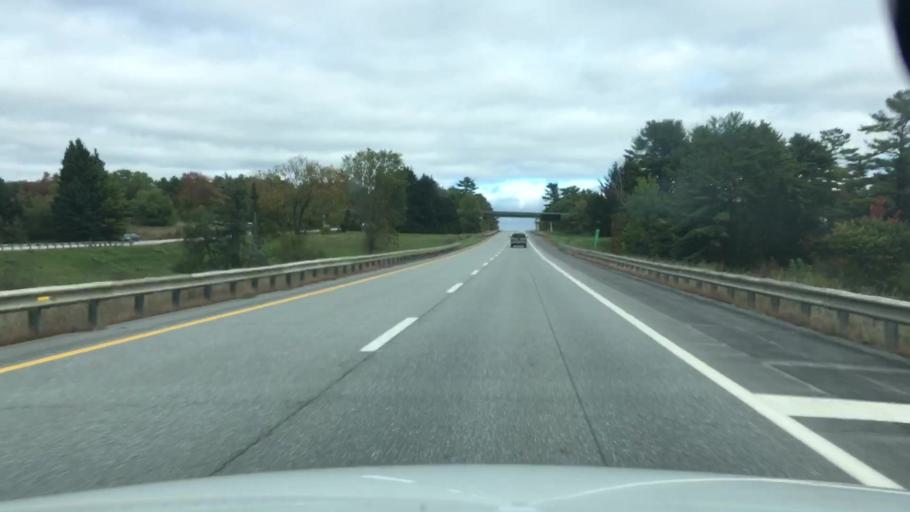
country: US
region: Maine
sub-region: Penobscot County
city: Carmel
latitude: 44.7787
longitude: -69.0657
